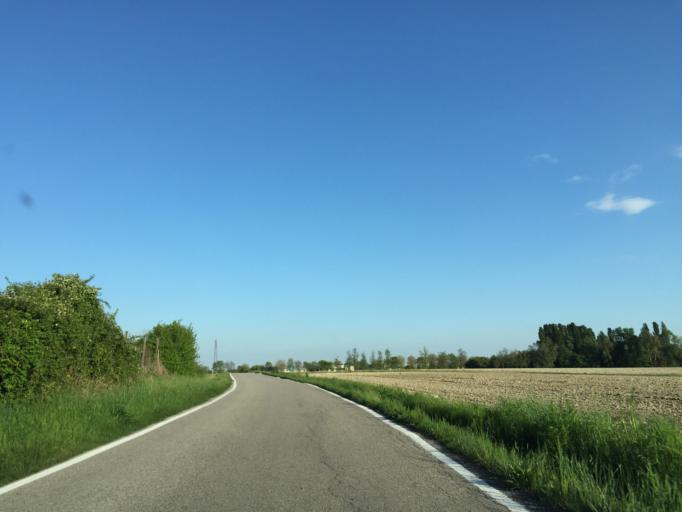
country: IT
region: Friuli Venezia Giulia
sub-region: Provincia di Pordenone
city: Tamai
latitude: 45.9604
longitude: 12.5770
